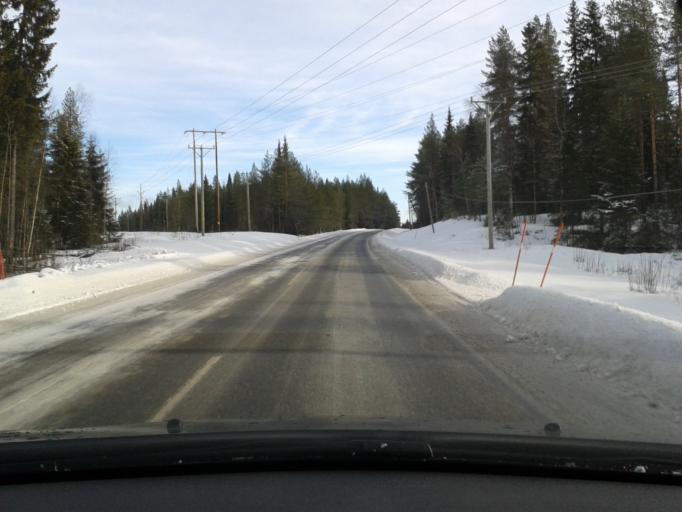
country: SE
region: Vaesterbotten
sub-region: Vilhelmina Kommun
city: Vilhelmina
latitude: 64.6471
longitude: 16.5411
